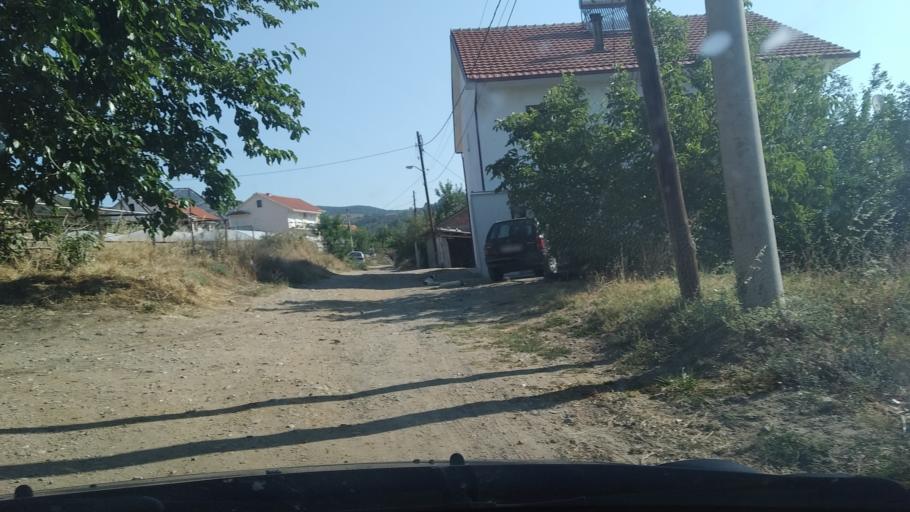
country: MK
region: Bogdanci
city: Bogdanci
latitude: 41.2059
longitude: 22.5822
